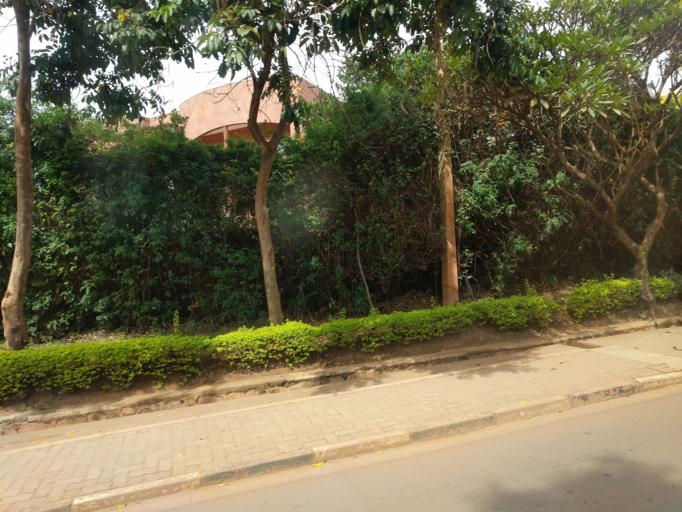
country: RW
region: Kigali
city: Kigali
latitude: -1.9738
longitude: 30.1043
